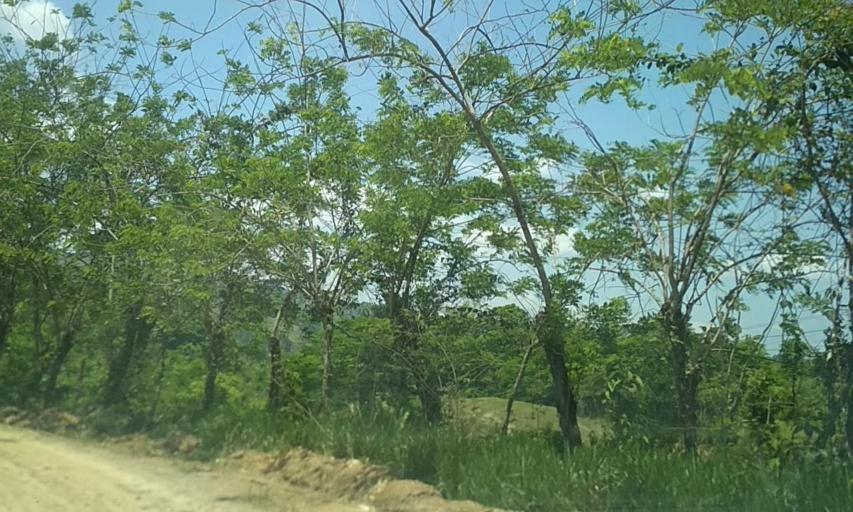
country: MX
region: Chiapas
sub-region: Tecpatan
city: Raudales Malpaso
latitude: 17.3954
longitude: -93.7244
